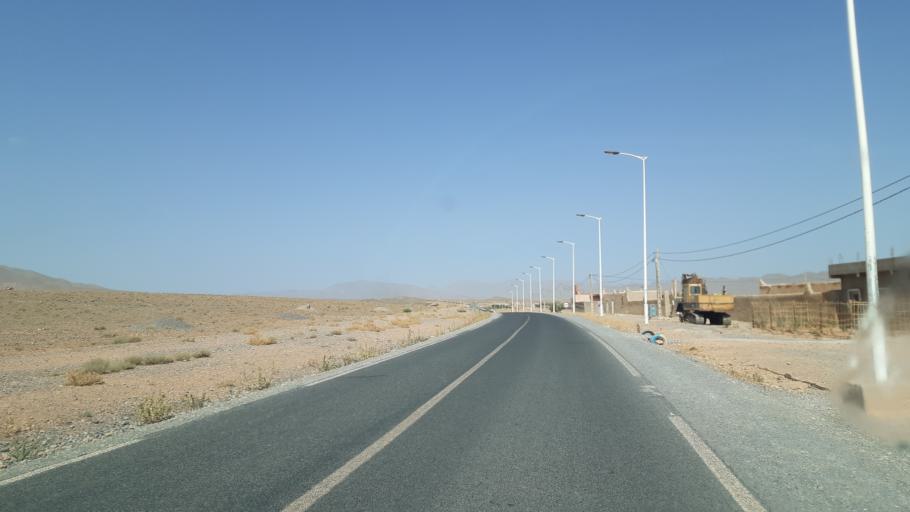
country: MA
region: Meknes-Tafilalet
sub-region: Errachidia
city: Amouguer
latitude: 32.2225
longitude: -4.6812
